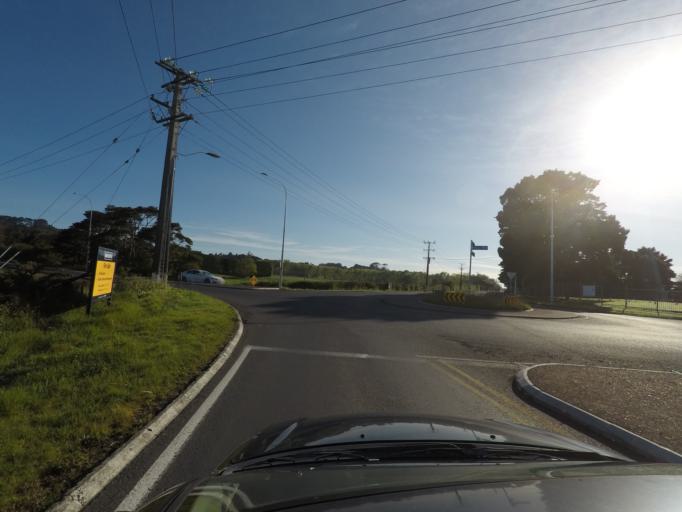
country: NZ
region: Auckland
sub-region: Auckland
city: Papakura
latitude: -37.0167
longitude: 174.9392
